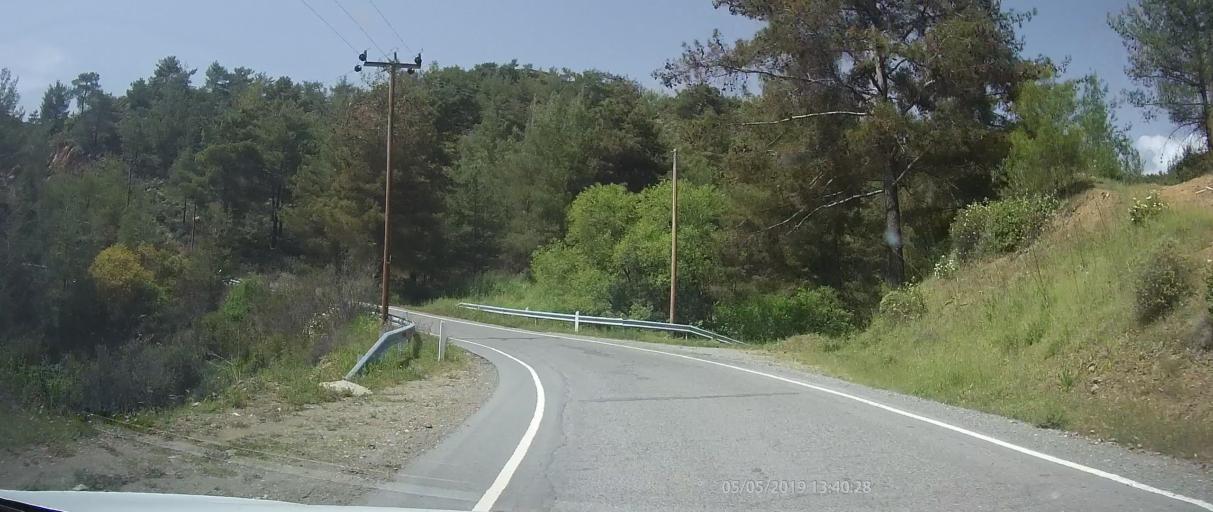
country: CY
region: Limassol
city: Pachna
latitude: 34.8717
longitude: 32.8261
